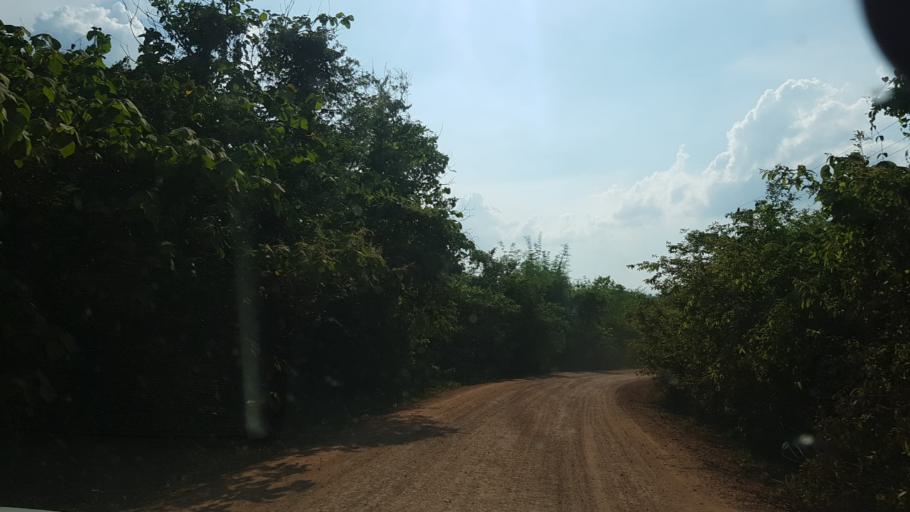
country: LA
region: Vientiane
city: Muang Phon-Hong
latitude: 18.3441
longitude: 102.2919
